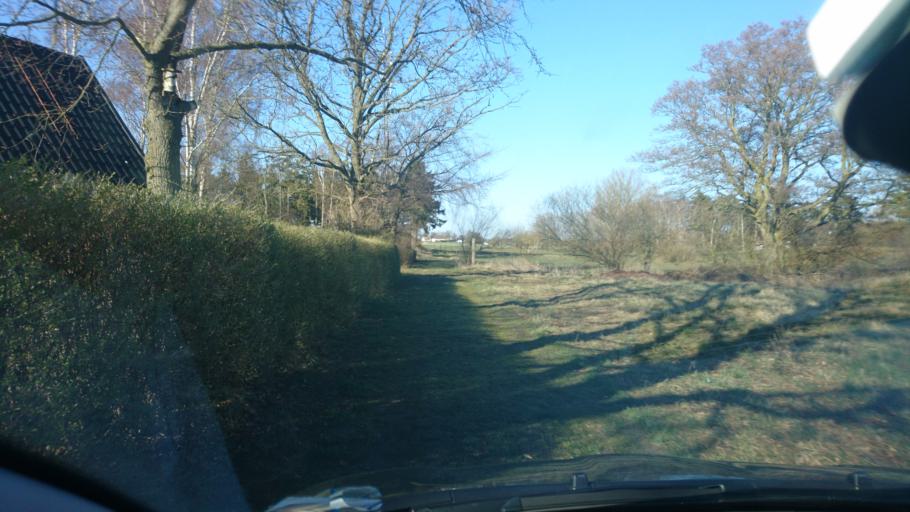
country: SE
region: Skane
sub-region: Simrishamns Kommun
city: Simrishamn
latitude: 55.4207
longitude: 14.2076
